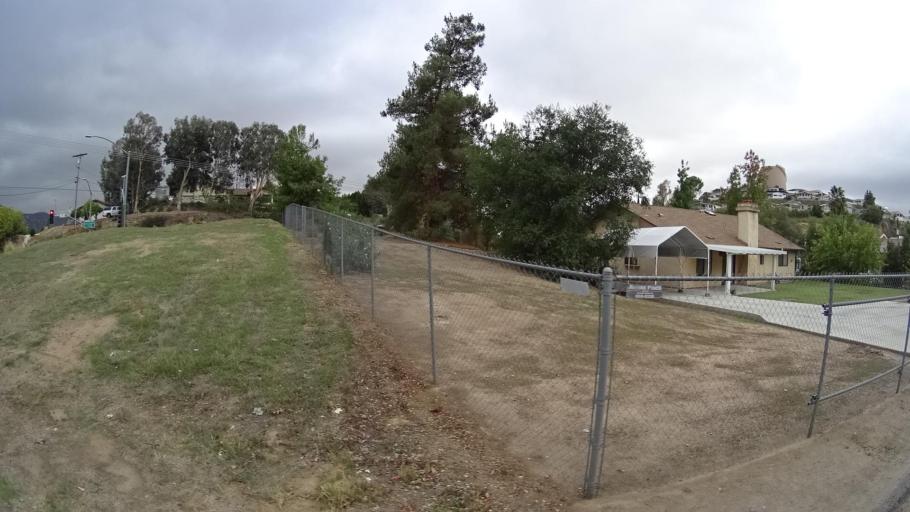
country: US
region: California
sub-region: San Diego County
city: Lakeside
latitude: 32.8482
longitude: -116.8835
